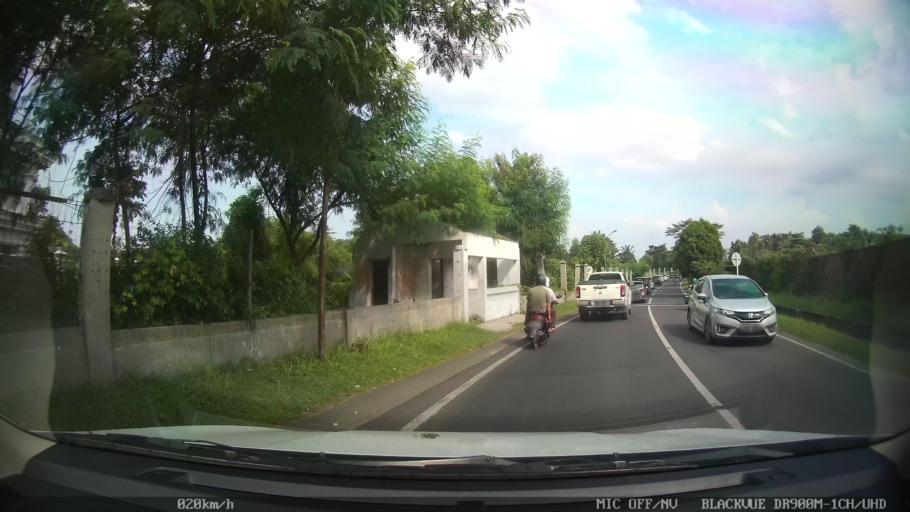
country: ID
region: North Sumatra
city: Medan
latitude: 3.5695
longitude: 98.6826
